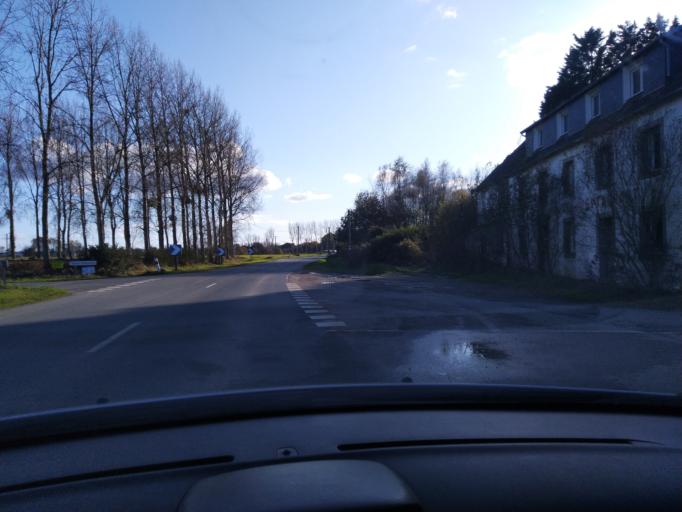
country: FR
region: Brittany
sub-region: Departement des Cotes-d'Armor
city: Plestin-les-Greves
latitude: 48.6272
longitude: -3.6165
